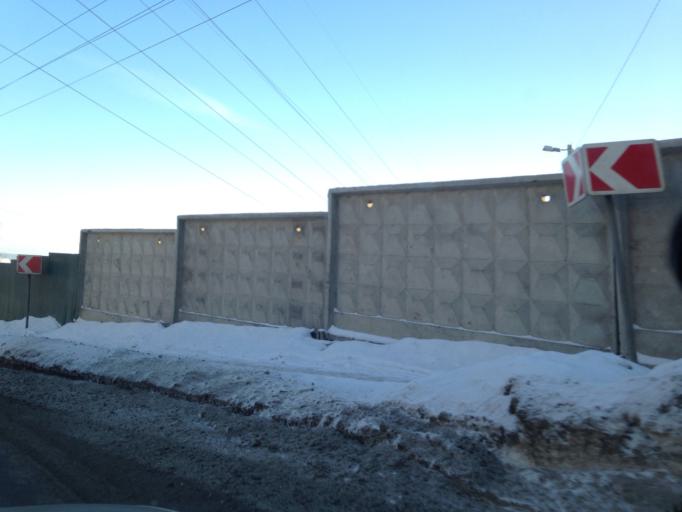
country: RU
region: Ulyanovsk
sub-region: Ulyanovskiy Rayon
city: Ulyanovsk
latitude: 54.3048
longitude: 48.3911
